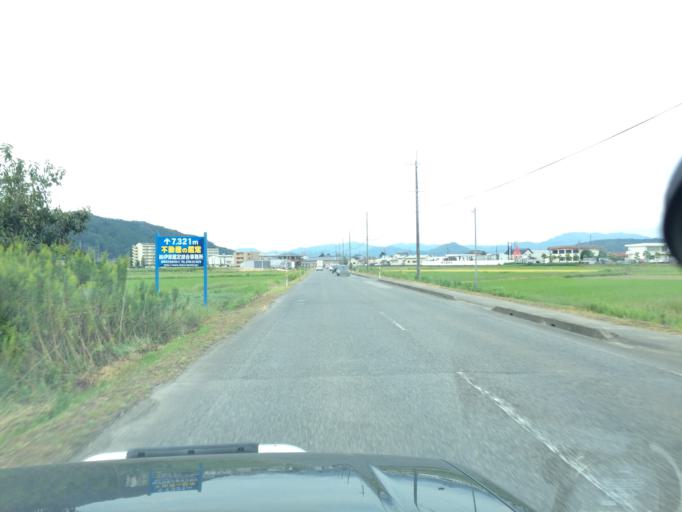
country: JP
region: Hyogo
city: Toyooka
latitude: 35.4904
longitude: 134.7970
